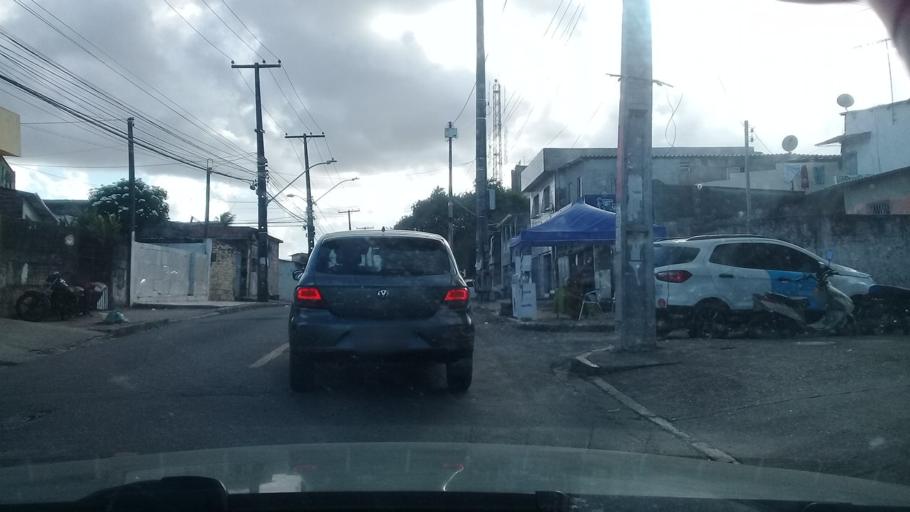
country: BR
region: Pernambuco
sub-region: Jaboatao Dos Guararapes
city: Jaboatao dos Guararapes
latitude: -8.1153
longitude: -34.9479
